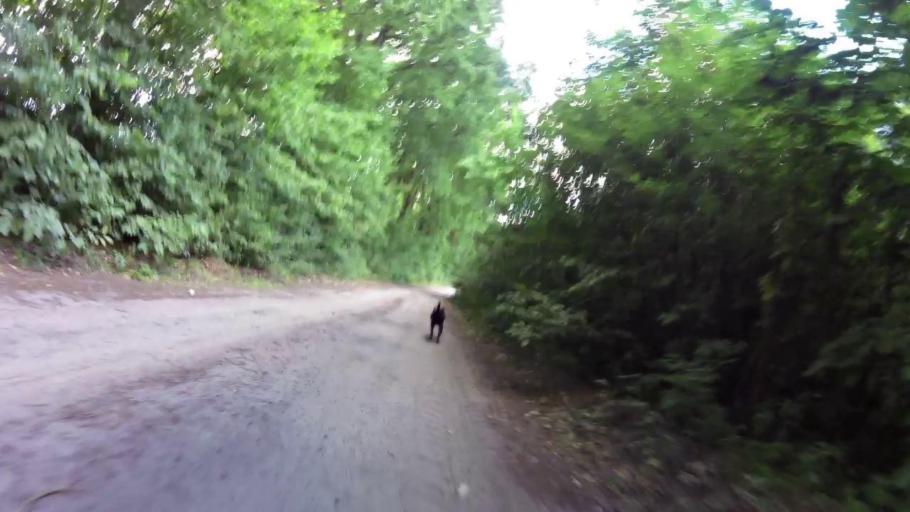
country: PL
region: West Pomeranian Voivodeship
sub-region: Powiat swidwinski
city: Swidwin
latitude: 53.6790
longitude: 15.7375
